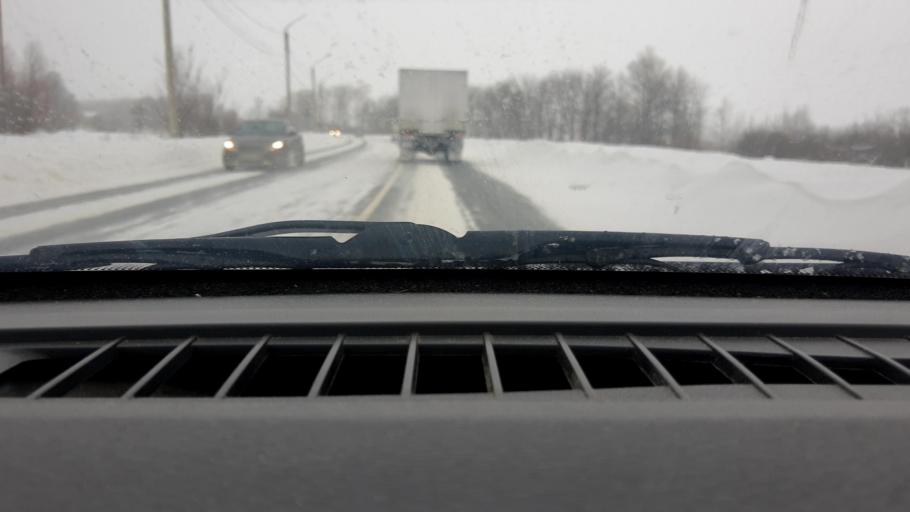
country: RU
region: Vladimir
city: Orgtrud
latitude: 56.2113
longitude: 40.5841
